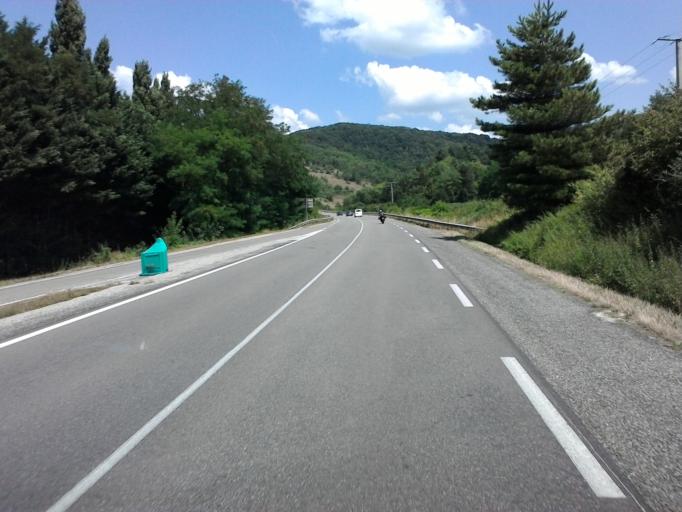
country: FR
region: Franche-Comte
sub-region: Departement du Jura
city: Cousance
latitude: 46.5256
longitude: 5.3933
